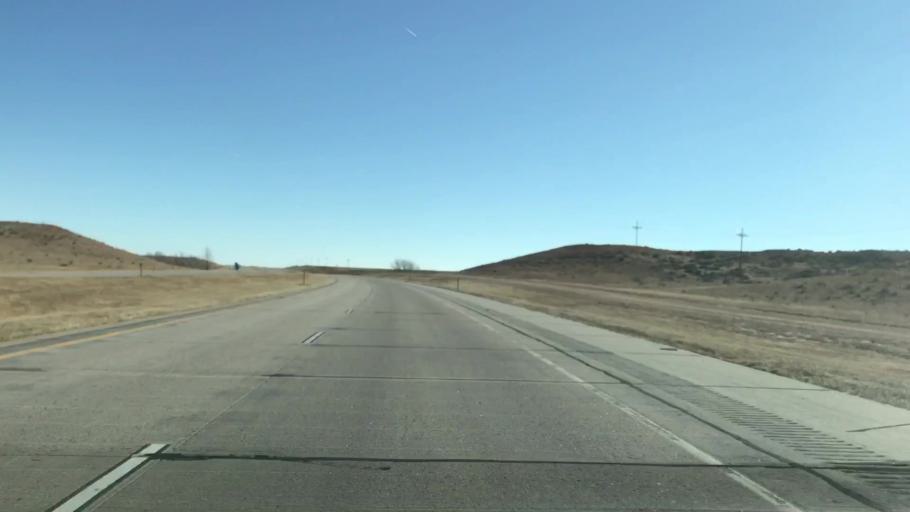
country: US
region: Colorado
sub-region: Lincoln County
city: Hugo
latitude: 39.2723
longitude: -102.9945
